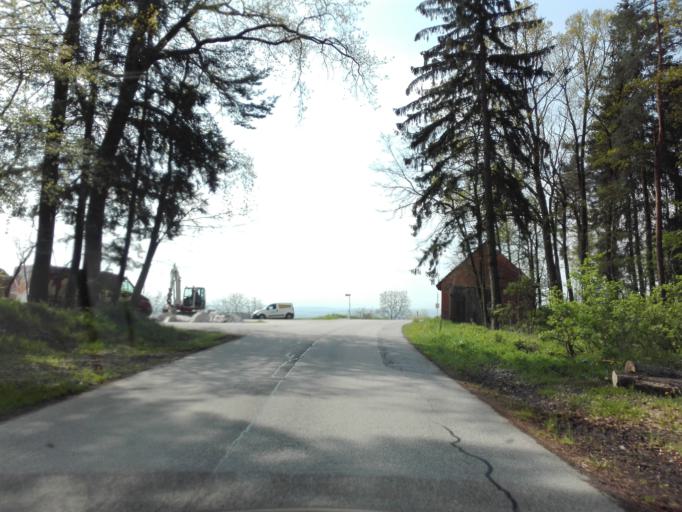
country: AT
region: Upper Austria
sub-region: Politischer Bezirk Perg
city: Perg
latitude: 48.2453
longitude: 14.7015
